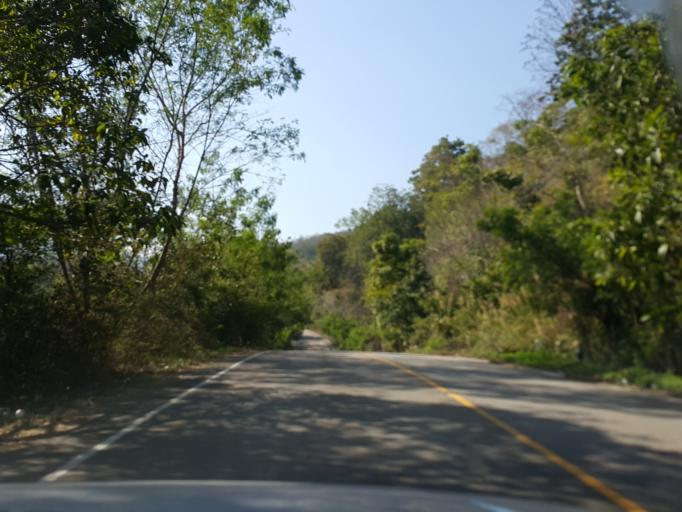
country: TH
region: Chiang Mai
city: Mae Wang
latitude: 18.6183
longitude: 98.7432
